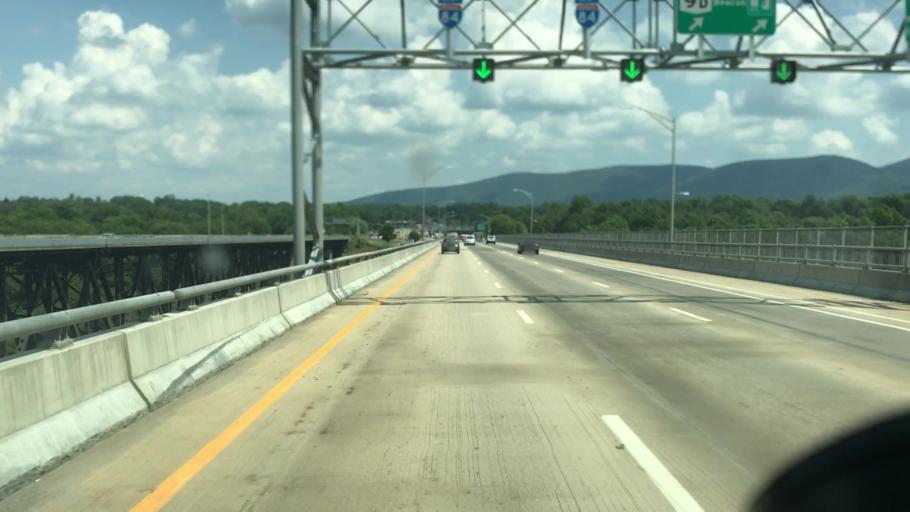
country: US
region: New York
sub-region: Dutchess County
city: Beacon
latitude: 41.5185
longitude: -73.9863
